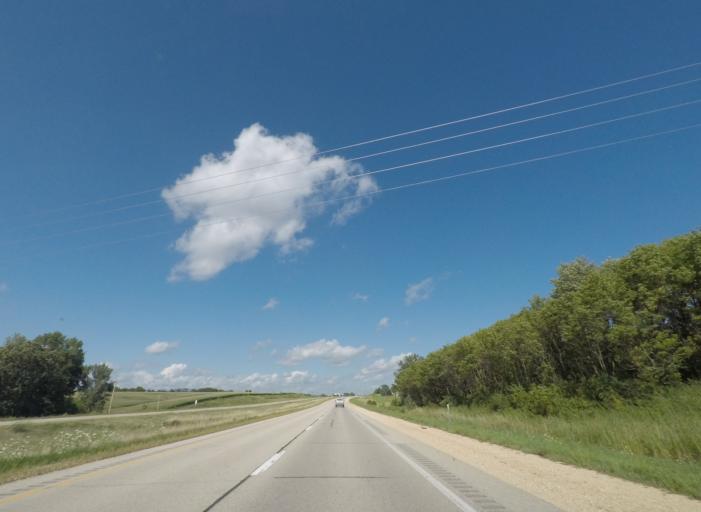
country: US
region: Iowa
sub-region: Dubuque County
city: Peosta
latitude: 42.3956
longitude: -90.7589
